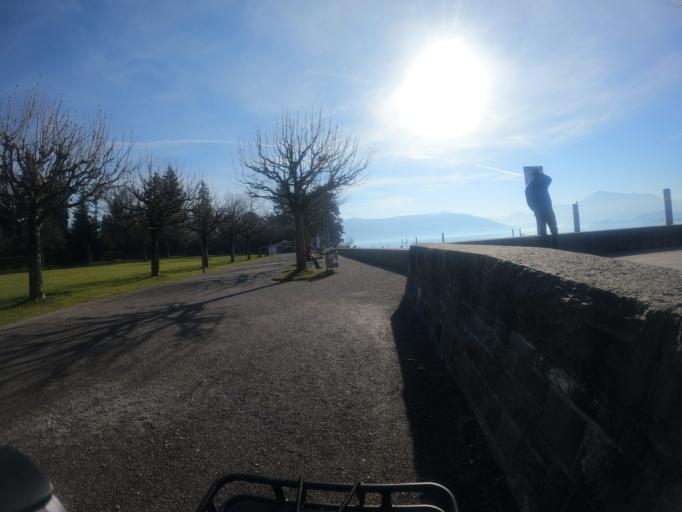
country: CH
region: Zug
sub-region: Zug
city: Cham
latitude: 47.1787
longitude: 8.4635
